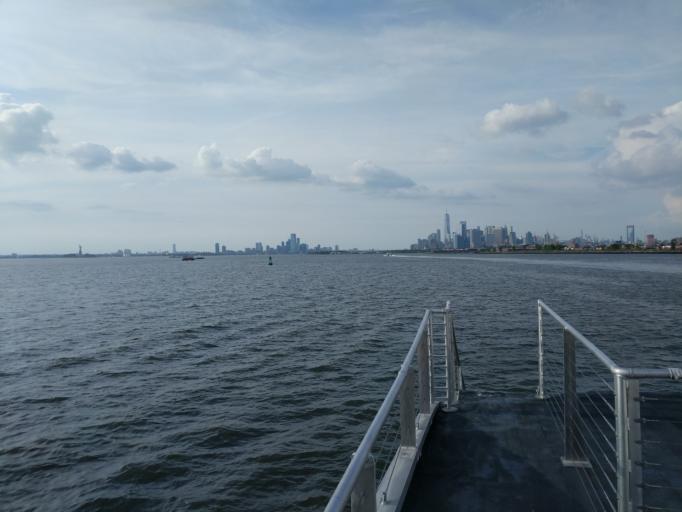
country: US
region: New York
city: New York City
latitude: 40.6610
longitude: -74.0216
